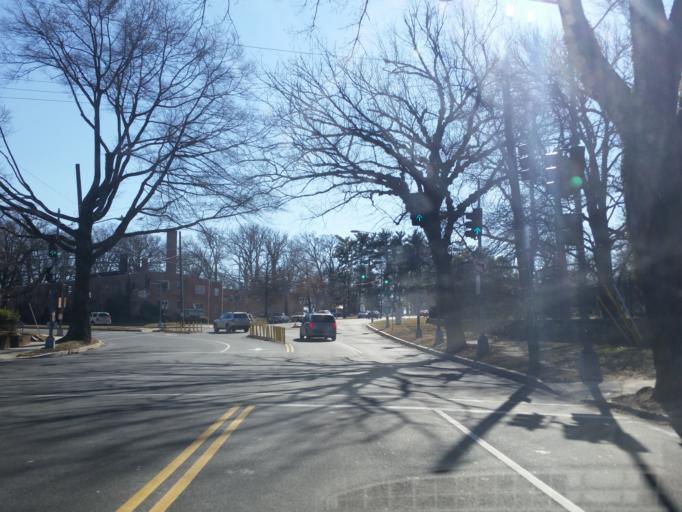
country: US
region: Maryland
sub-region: Prince George's County
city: Chillum
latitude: 38.9476
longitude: -77.0087
